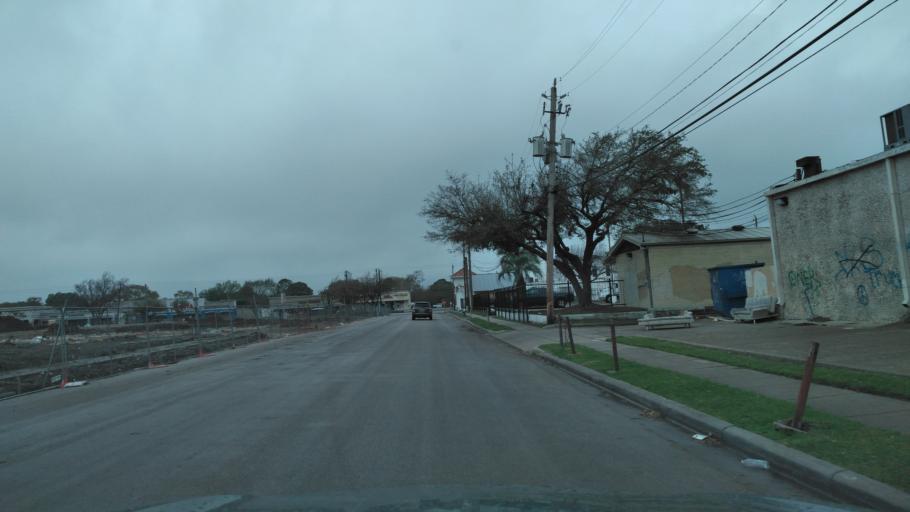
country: US
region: Texas
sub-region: Harris County
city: Piney Point Village
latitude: 29.7305
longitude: -95.4993
